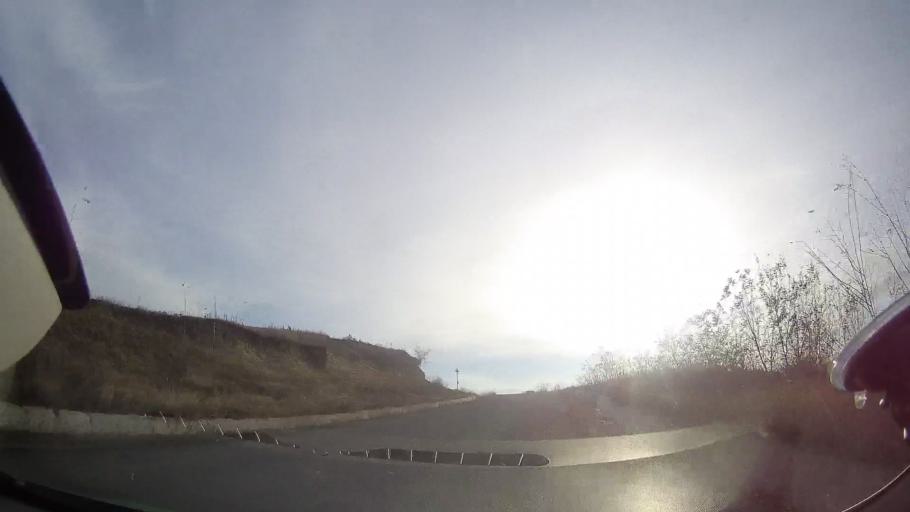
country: RO
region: Bihor
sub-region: Comuna Sarbi
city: Burzuc
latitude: 47.1309
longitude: 22.1871
